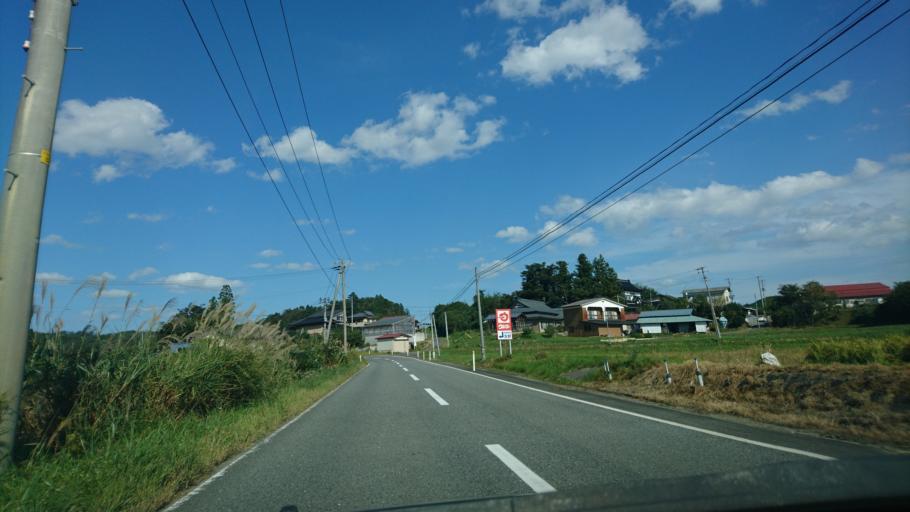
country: JP
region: Iwate
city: Ichinoseki
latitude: 38.8429
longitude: 141.0280
